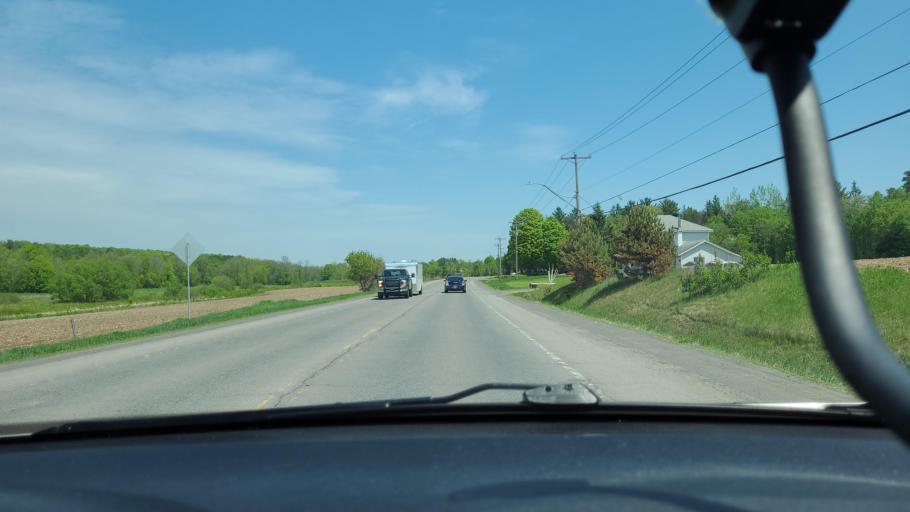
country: CA
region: Quebec
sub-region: Laurentides
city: Lachute
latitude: 45.6674
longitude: -74.2804
